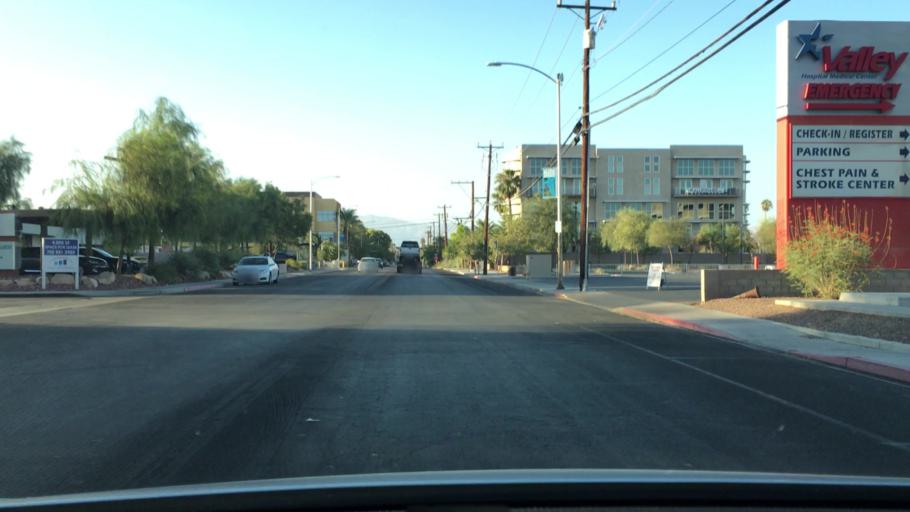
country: US
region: Nevada
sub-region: Clark County
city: Las Vegas
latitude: 36.1623
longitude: -115.1700
